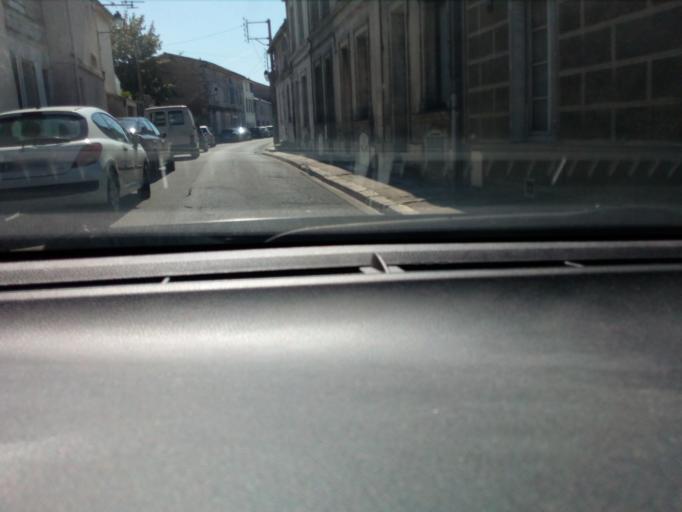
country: FR
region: Poitou-Charentes
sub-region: Departement de la Charente
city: Angouleme
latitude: 45.6601
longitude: 0.1617
